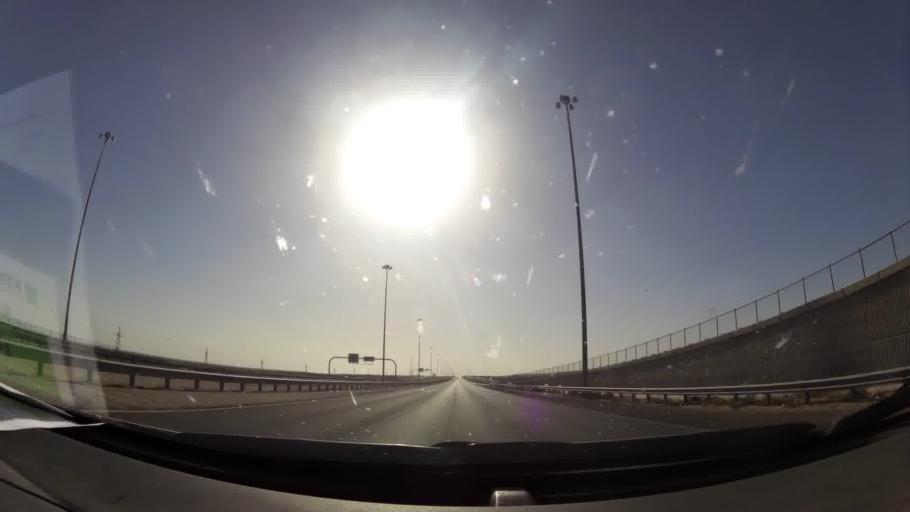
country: KW
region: Al Asimah
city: Kuwait City
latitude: 29.5716
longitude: 47.8979
